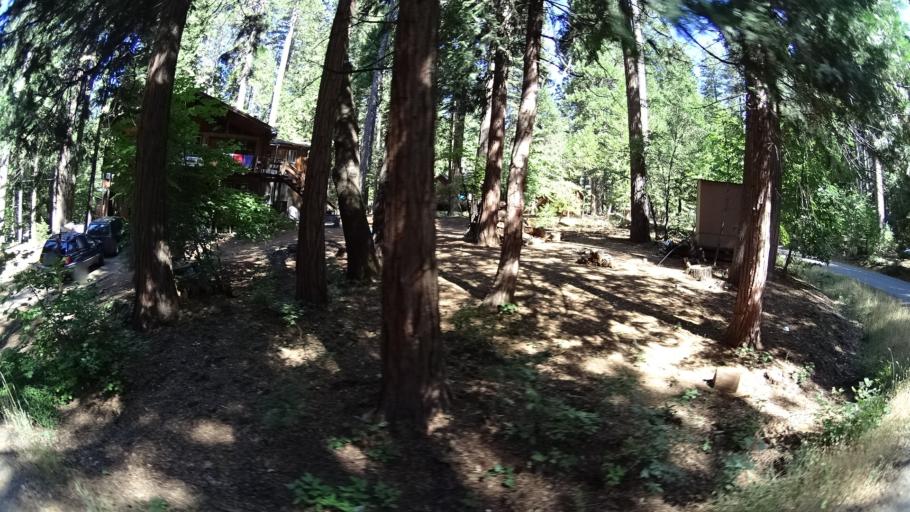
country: US
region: California
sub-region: Calaveras County
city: Arnold
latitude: 38.2414
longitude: -120.3271
